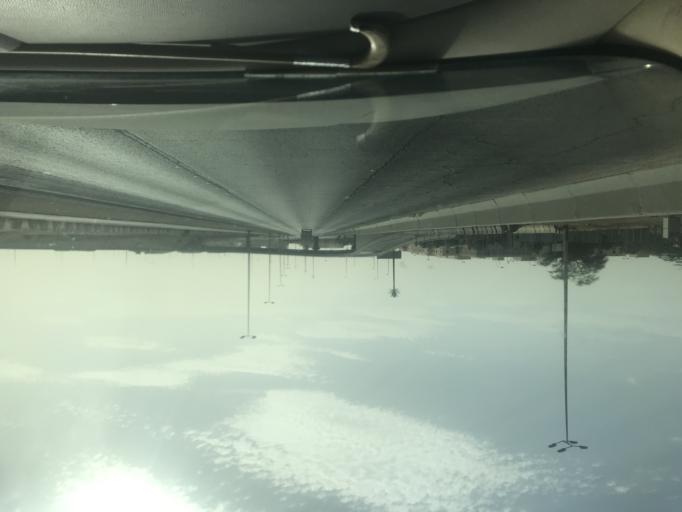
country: SA
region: Ar Riyad
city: Riyadh
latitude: 24.8224
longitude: 46.7121
